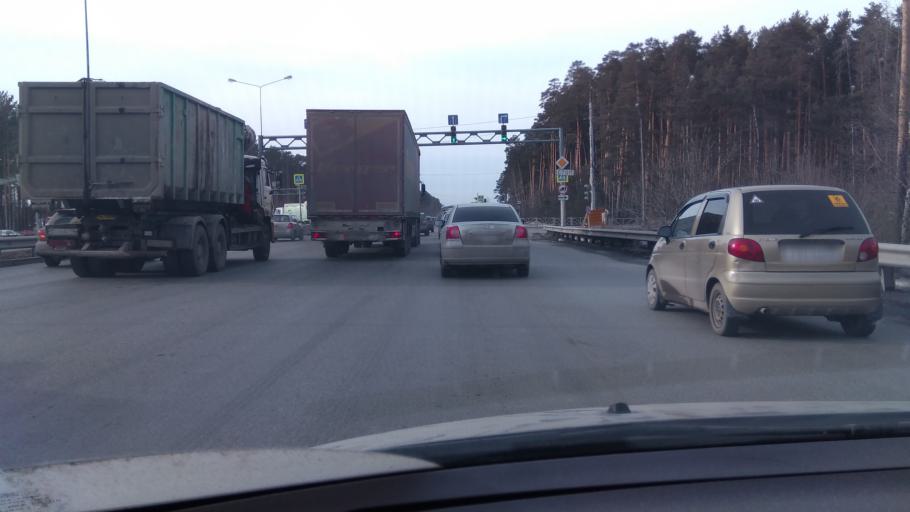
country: RU
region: Sverdlovsk
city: Shirokaya Rechka
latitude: 56.8126
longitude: 60.5187
